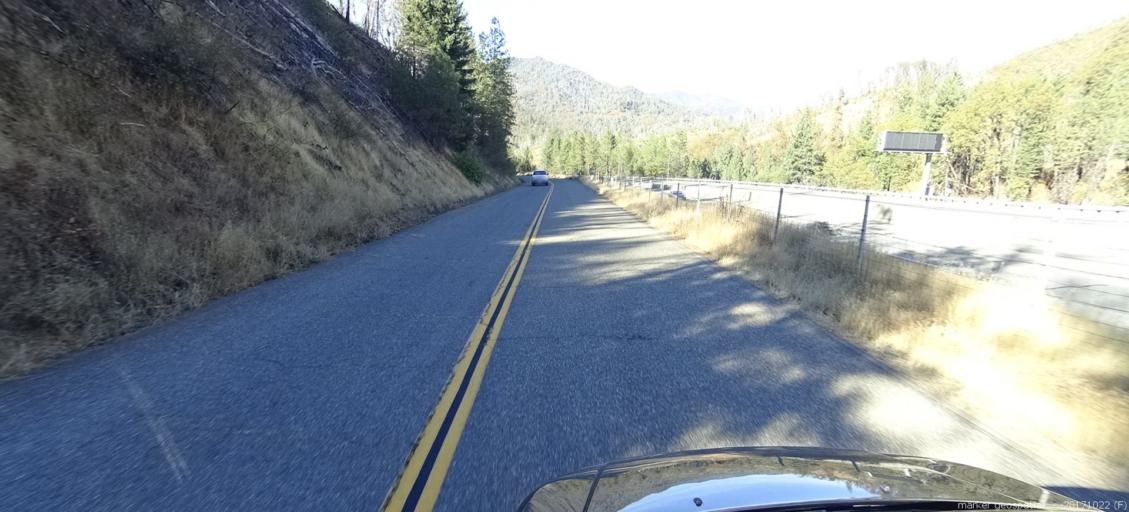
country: US
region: California
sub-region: Shasta County
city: Shasta Lake
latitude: 40.8410
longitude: -122.3284
